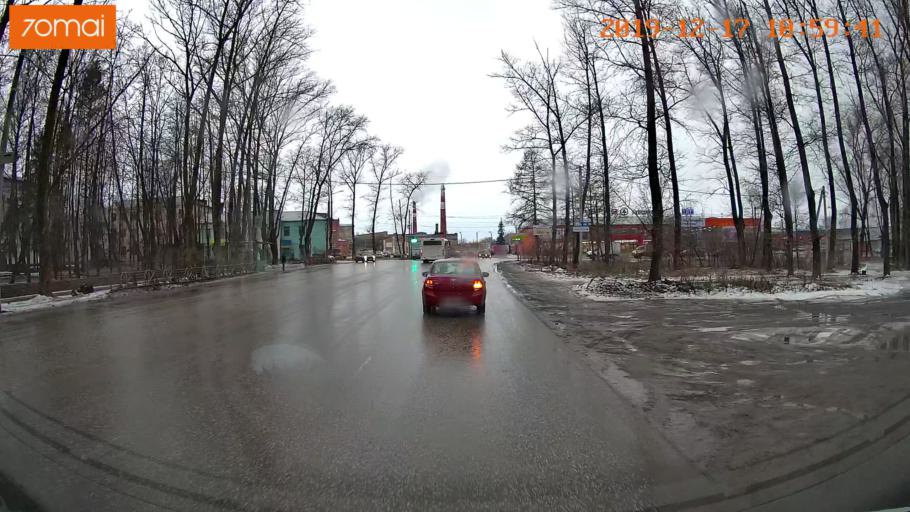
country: RU
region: Vladimir
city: Gus'-Khrustal'nyy
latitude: 55.6221
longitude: 40.6448
